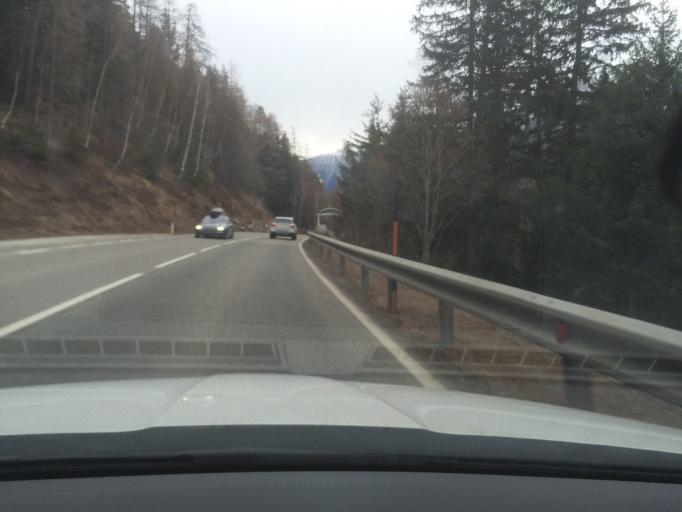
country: AT
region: Tyrol
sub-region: Politischer Bezirk Lienz
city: Matrei in Osttirol
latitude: 47.0130
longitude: 12.5390
